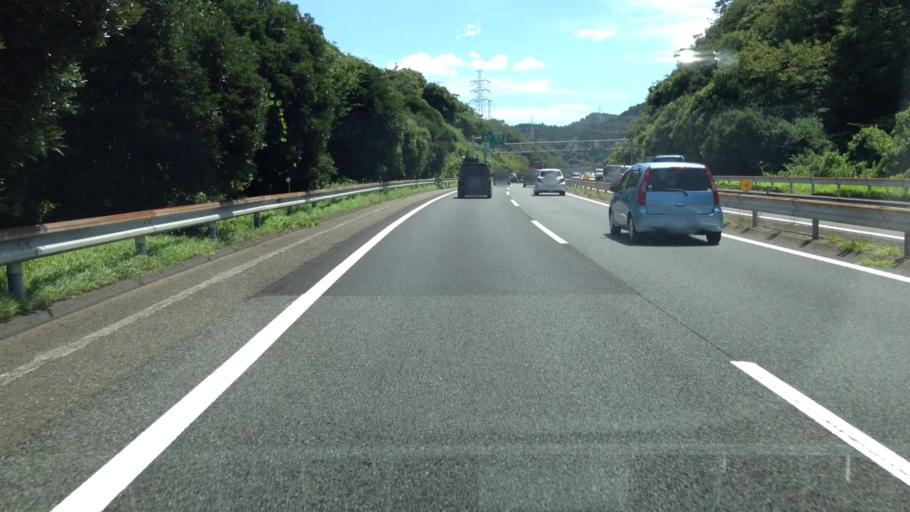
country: JP
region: Kanagawa
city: Zushi
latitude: 35.2997
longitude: 139.6161
